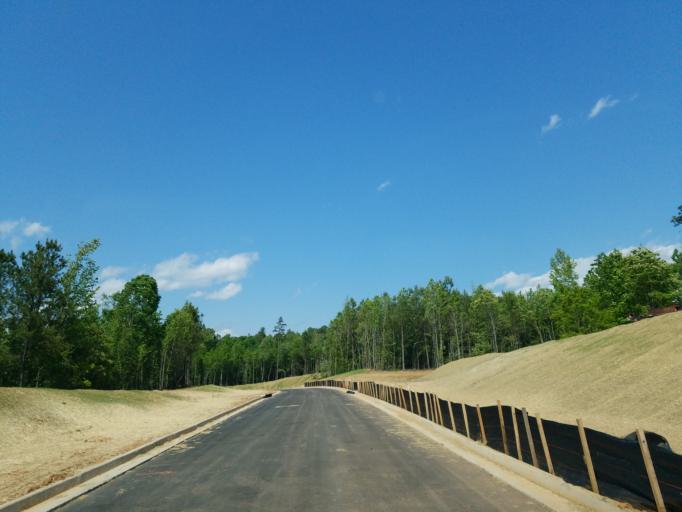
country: US
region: Georgia
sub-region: Fulton County
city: Milton
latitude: 34.2098
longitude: -84.2849
